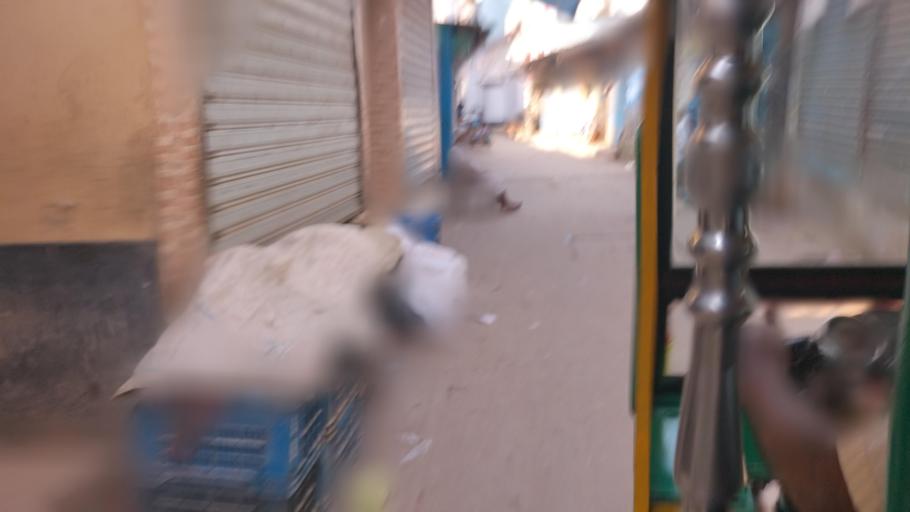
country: BD
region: Dhaka
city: Azimpur
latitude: 23.7965
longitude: 90.3379
